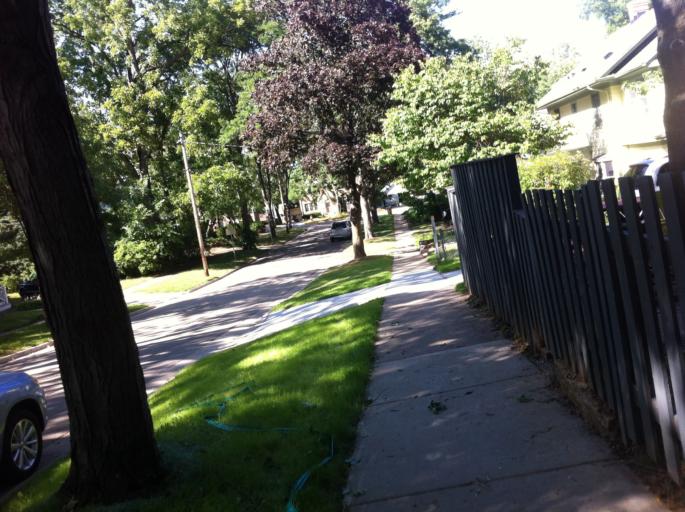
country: US
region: Wisconsin
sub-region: Dane County
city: Shorewood Hills
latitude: 43.0699
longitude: -89.4260
